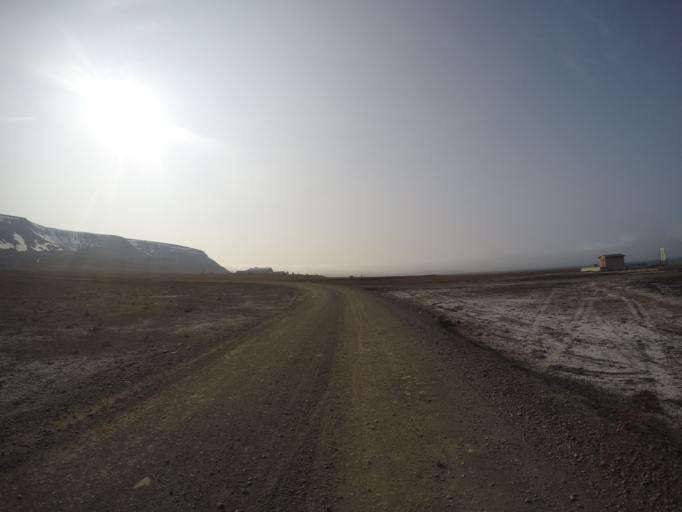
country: SJ
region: Svalbard
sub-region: Spitsbergen
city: Longyearbyen
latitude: 78.2475
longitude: 15.5361
